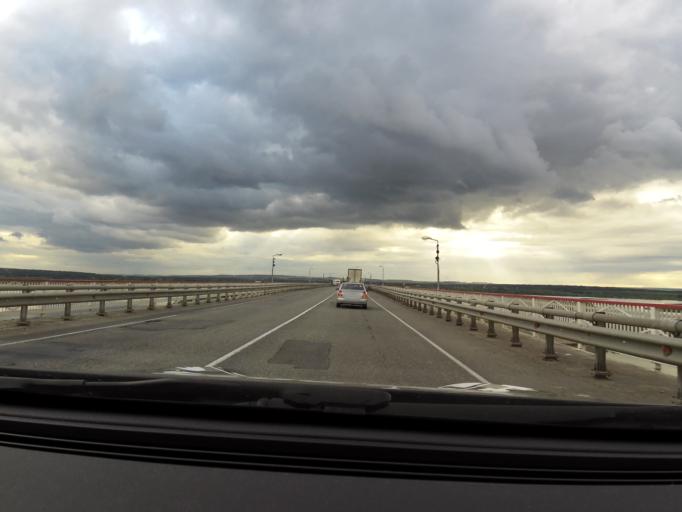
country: RU
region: Tatarstan
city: Sviyazhsk
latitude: 55.7189
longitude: 48.5922
